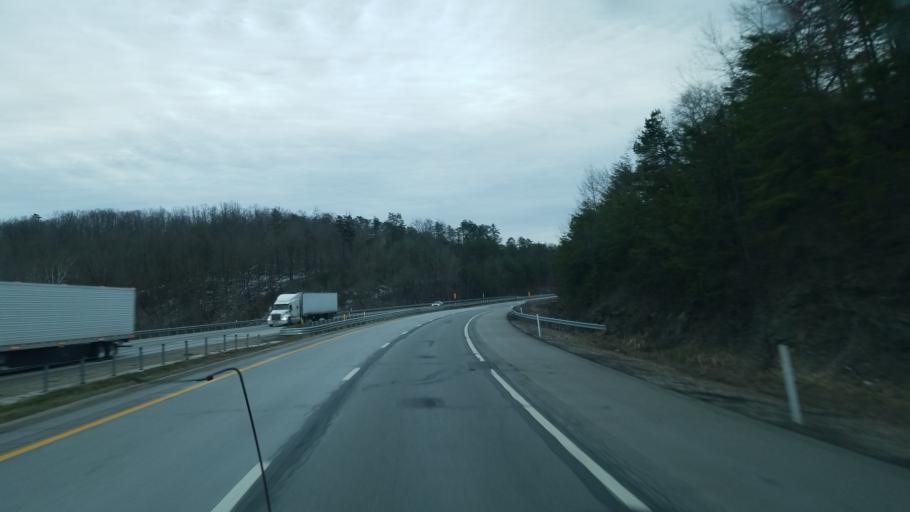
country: US
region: West Virginia
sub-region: Jackson County
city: Ravenswood
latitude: 38.9024
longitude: -81.7238
